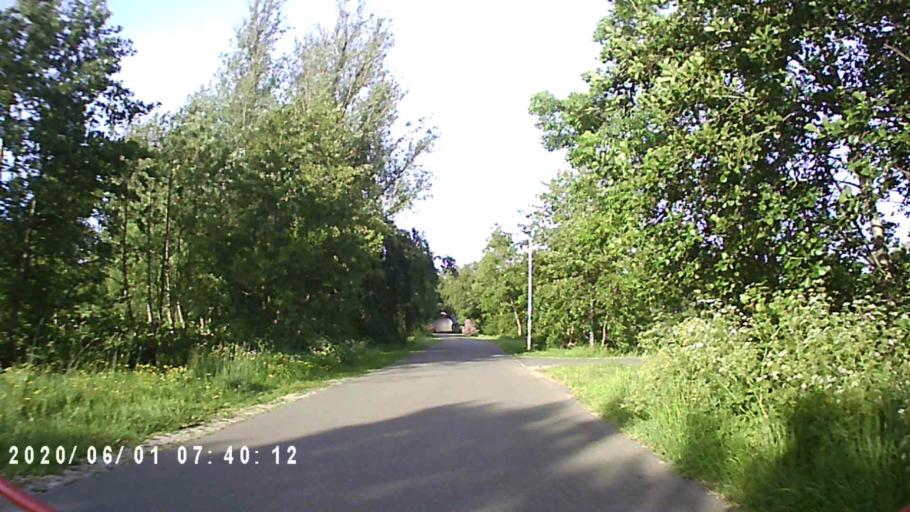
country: NL
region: Friesland
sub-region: Gemeente Dantumadiel
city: Damwald
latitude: 53.2947
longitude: 5.9894
